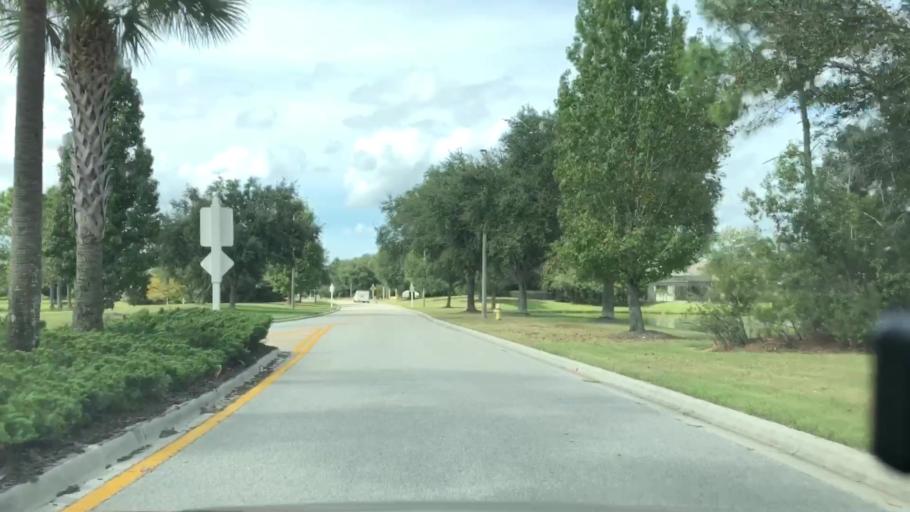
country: US
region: Florida
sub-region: Sarasota County
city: The Meadows
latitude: 27.4254
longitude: -82.3992
